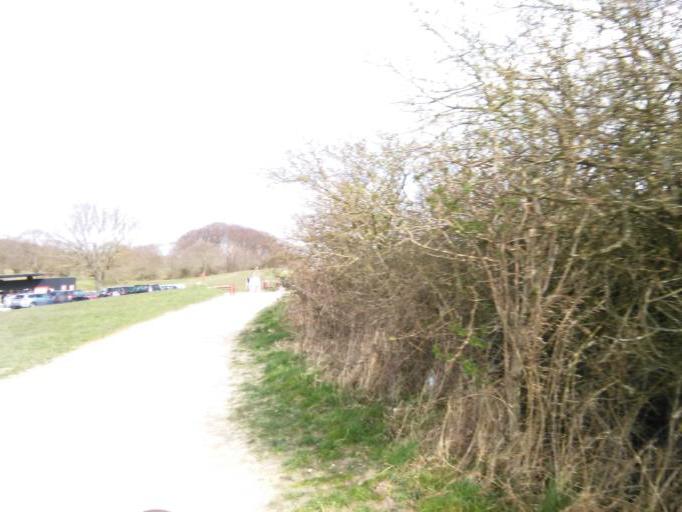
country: DK
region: Central Jutland
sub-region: Arhus Kommune
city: Beder
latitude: 56.0882
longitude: 10.2483
